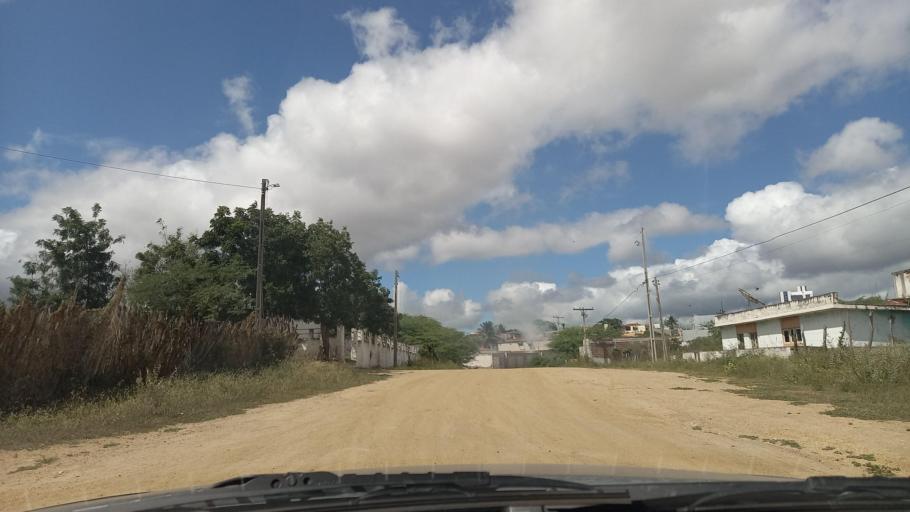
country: BR
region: Pernambuco
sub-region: Caruaru
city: Caruaru
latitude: -8.2532
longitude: -35.9812
